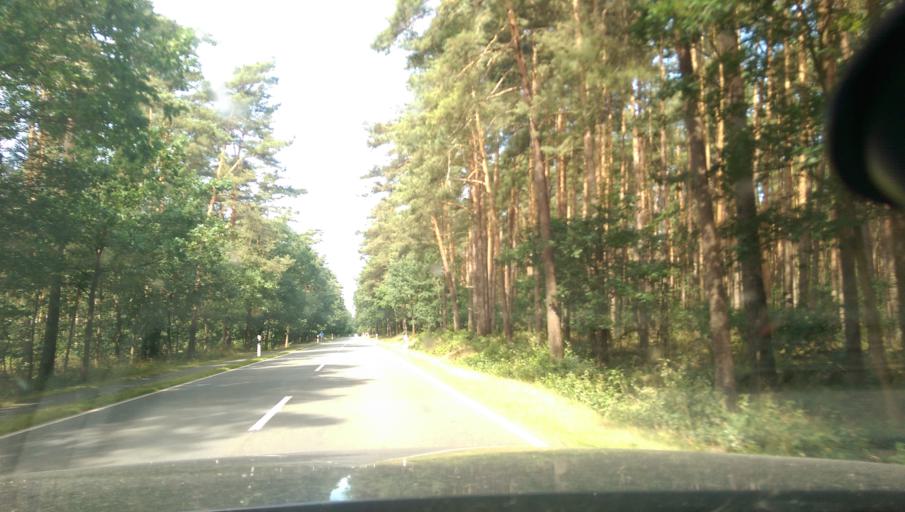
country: DE
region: Lower Saxony
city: Wietze
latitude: 52.6746
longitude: 9.8558
